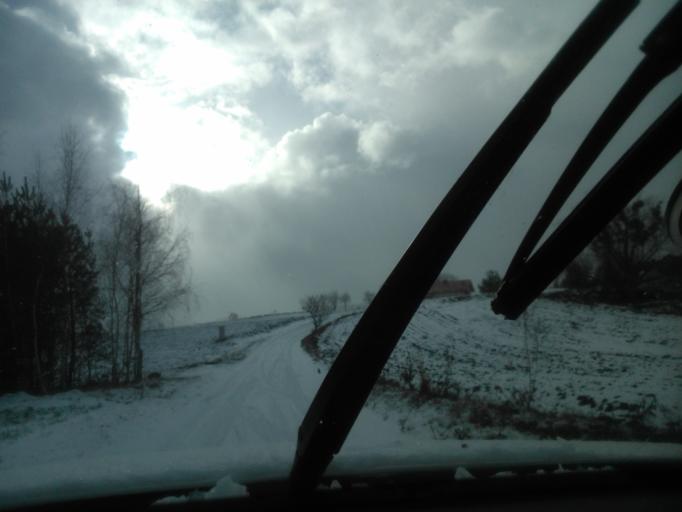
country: PL
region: Kujawsko-Pomorskie
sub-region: Powiat brodnicki
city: Bobrowo
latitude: 53.3115
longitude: 19.2493
